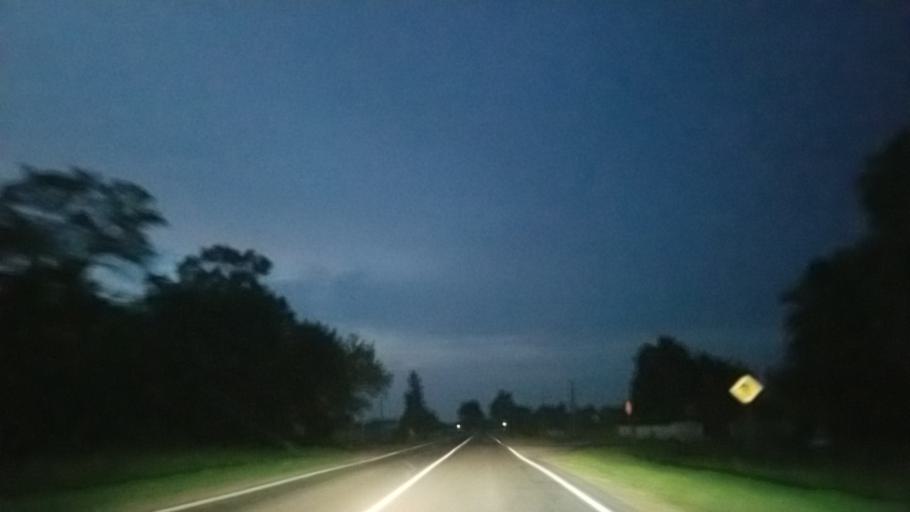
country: PL
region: Lublin Voivodeship
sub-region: Powiat bialski
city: Koden
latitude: 51.9204
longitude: 23.6601
